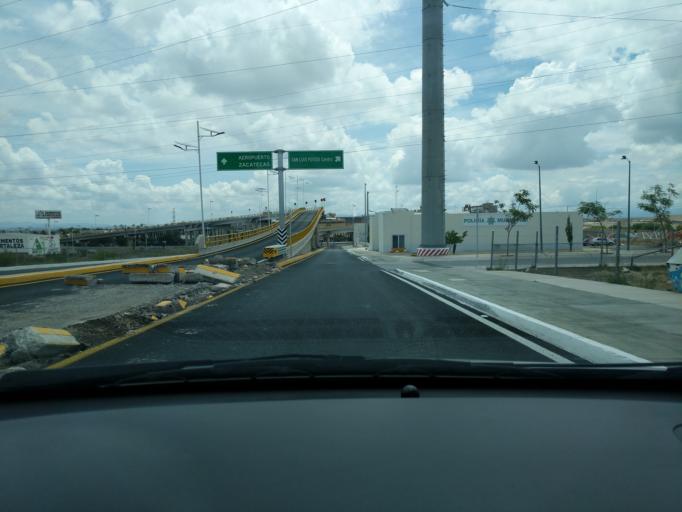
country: MX
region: San Luis Potosi
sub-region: Mexquitic de Carmona
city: Guadalupe Victoria
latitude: 22.1691
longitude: -101.0423
